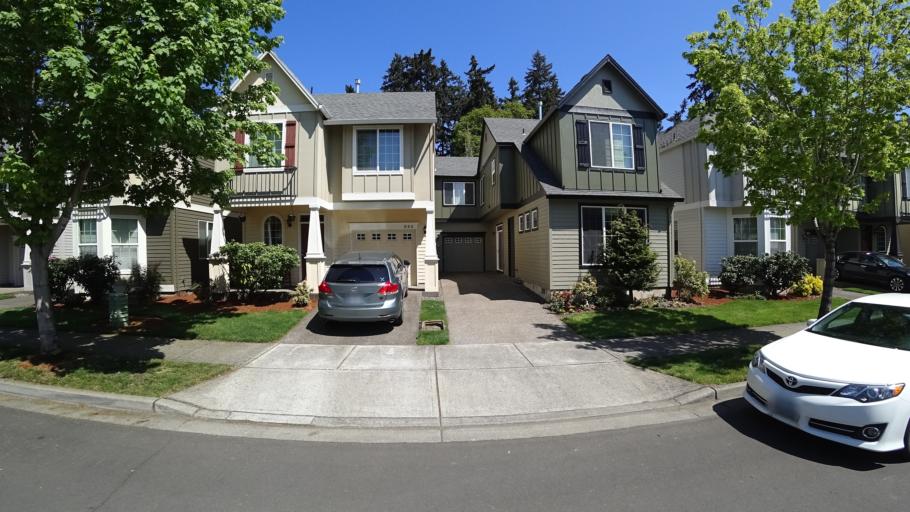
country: US
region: Oregon
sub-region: Washington County
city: Hillsboro
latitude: 45.5121
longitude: -122.9757
